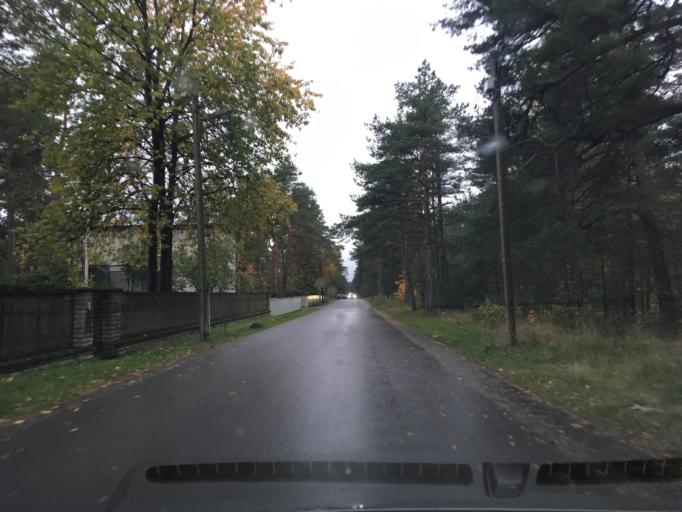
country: EE
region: Harju
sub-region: Saue vald
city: Laagri
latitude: 59.3786
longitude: 24.6862
